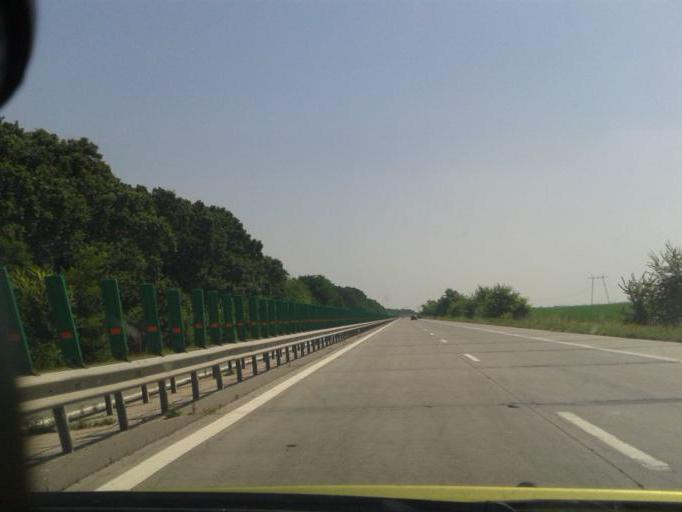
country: RO
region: Calarasi
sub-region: Comuna Belciugatele
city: Belciugatele
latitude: 44.4478
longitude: 26.4349
